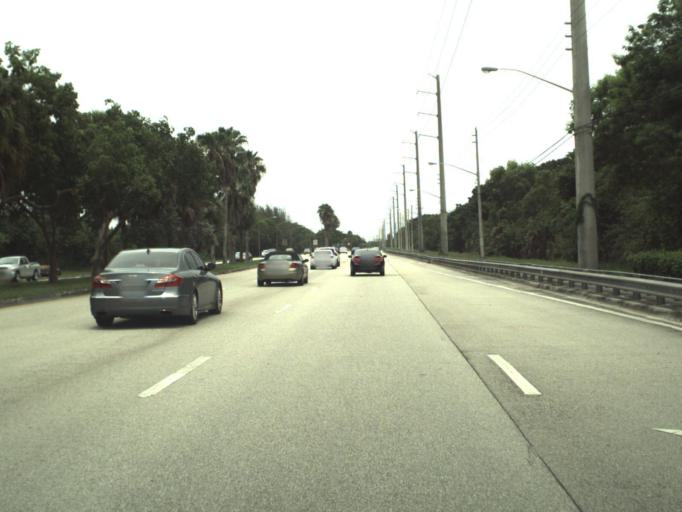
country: US
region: Florida
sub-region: Palm Beach County
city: Boca Pointe
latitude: 26.3493
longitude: -80.1849
